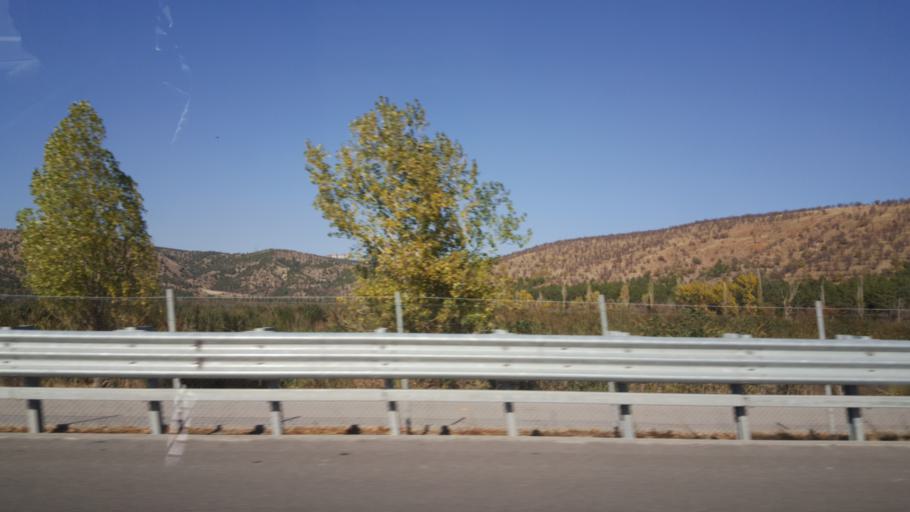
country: TR
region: Ankara
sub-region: Goelbasi
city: Golbasi
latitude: 39.8133
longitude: 32.8190
